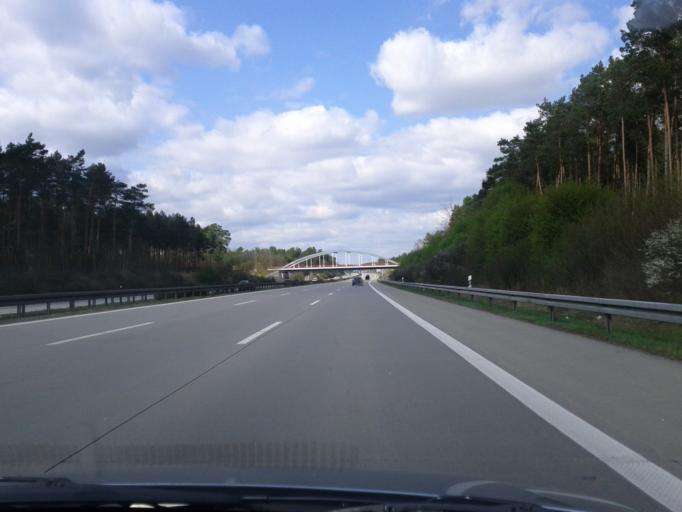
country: DE
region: Brandenburg
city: Grunheide
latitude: 52.4057
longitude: 13.7864
